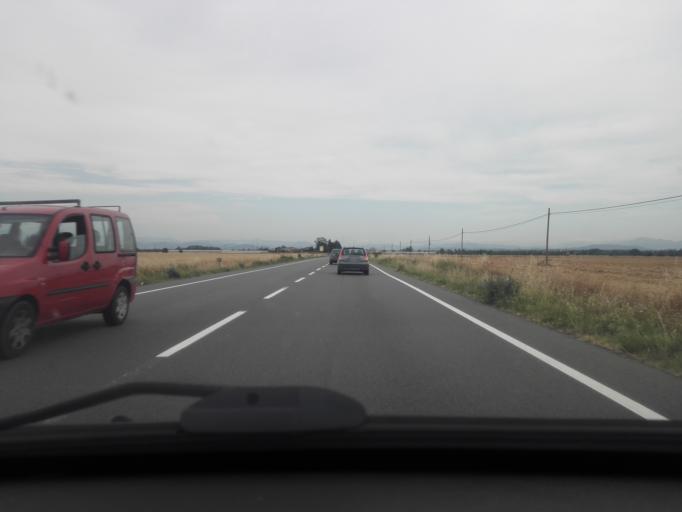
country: IT
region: Piedmont
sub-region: Provincia di Alessandria
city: Pozzolo Formigaro
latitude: 44.8173
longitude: 8.7567
